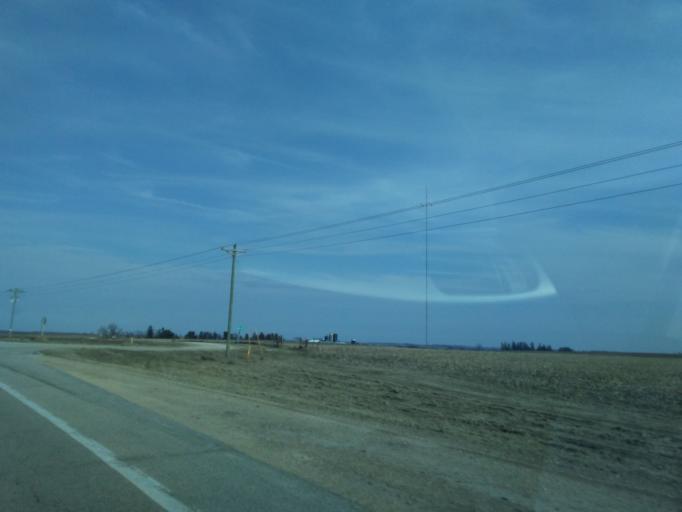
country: US
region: Wisconsin
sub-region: Grant County
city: Lancaster
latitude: 42.9600
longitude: -90.9170
